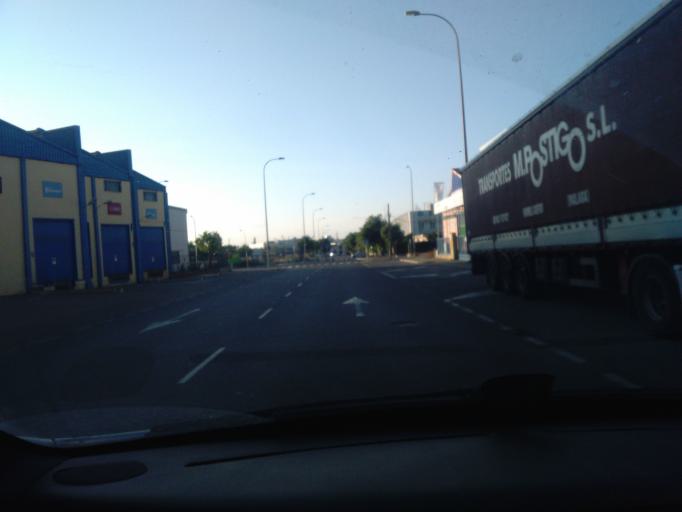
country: ES
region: Andalusia
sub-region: Provincia de Sevilla
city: Sevilla
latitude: 37.3917
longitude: -5.9457
